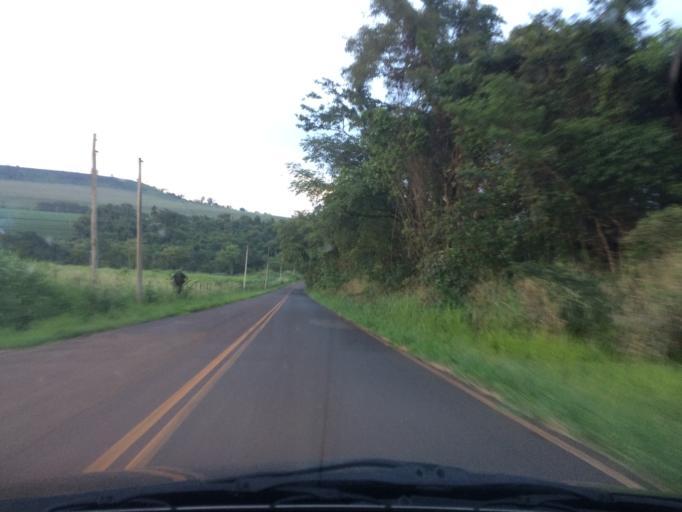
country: BR
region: Sao Paulo
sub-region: Tambau
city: Tambau
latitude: -21.7232
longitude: -47.1883
